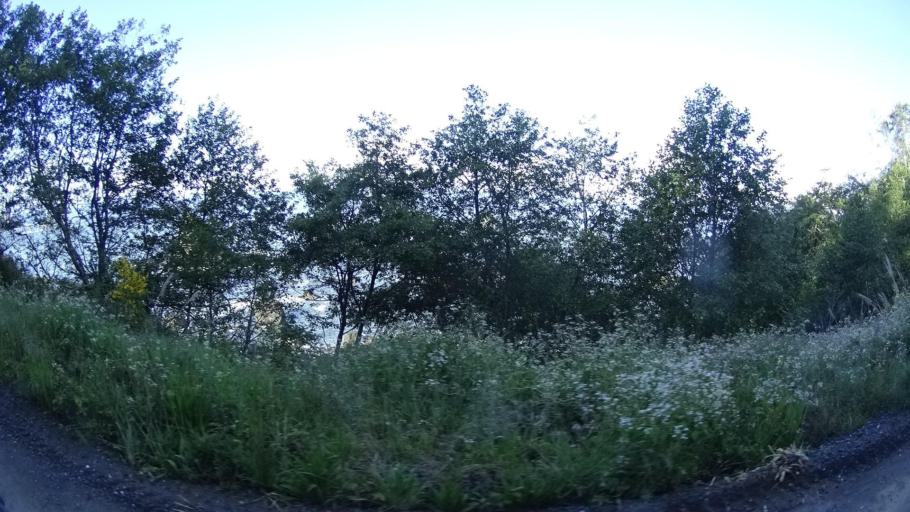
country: US
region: California
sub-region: Humboldt County
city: Westhaven-Moonstone
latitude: 41.0451
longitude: -124.1226
